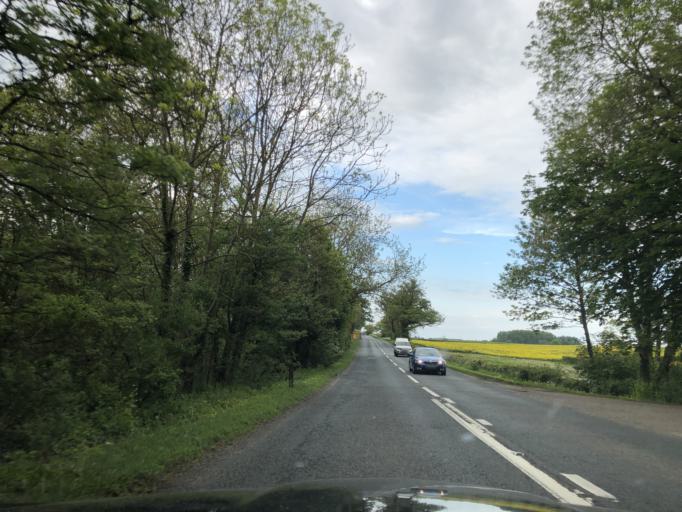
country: GB
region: England
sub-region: Gloucestershire
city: Donnington
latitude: 51.9616
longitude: -1.7117
